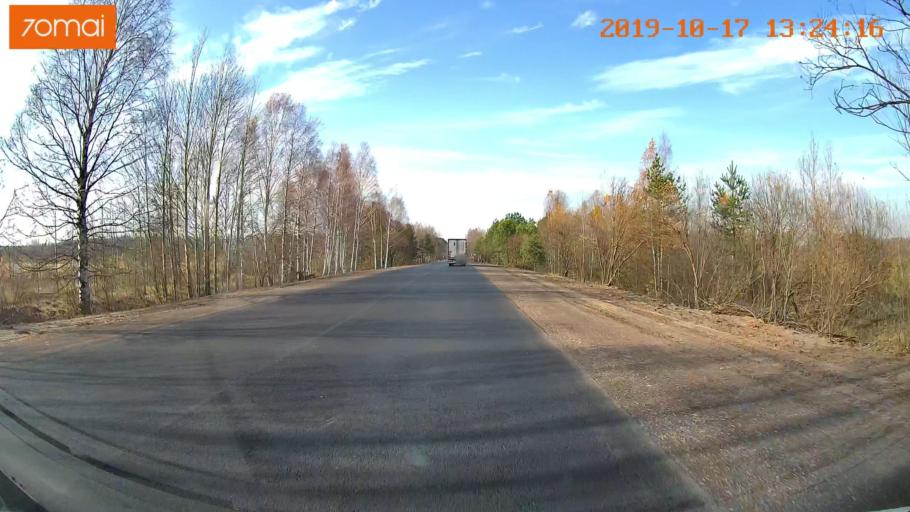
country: RU
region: Rjazan
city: Gus'-Zheleznyy
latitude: 55.0943
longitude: 40.9663
